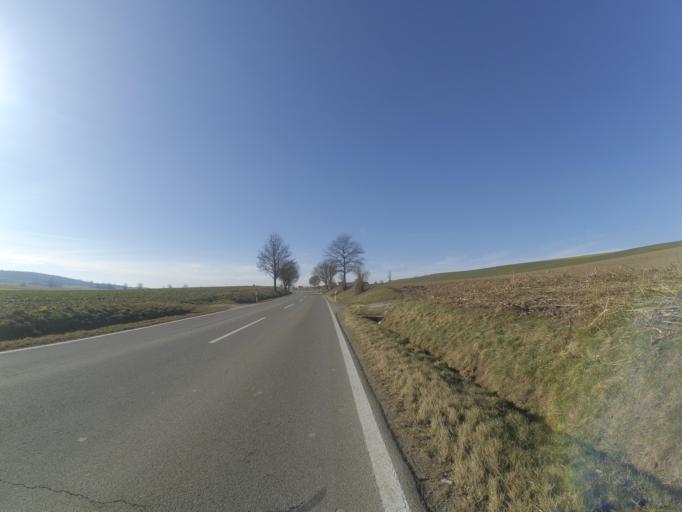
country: DE
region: Baden-Wuerttemberg
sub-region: Tuebingen Region
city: Aulendorf
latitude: 47.9239
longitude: 9.6321
